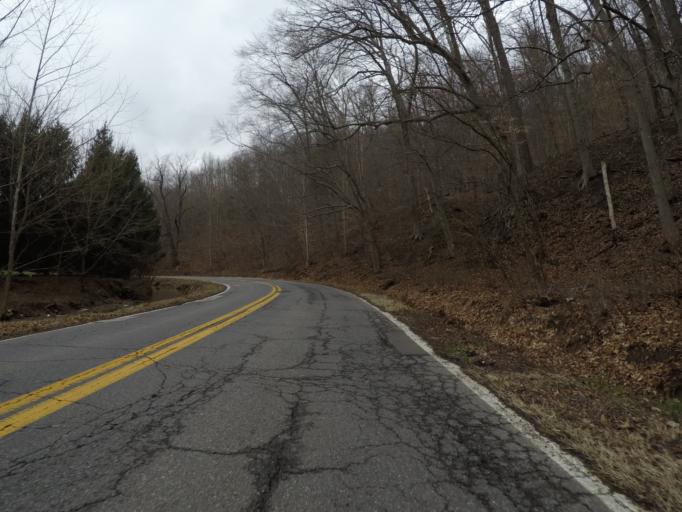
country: US
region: West Virginia
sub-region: Cabell County
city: Lesage
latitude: 38.4704
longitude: -82.2826
